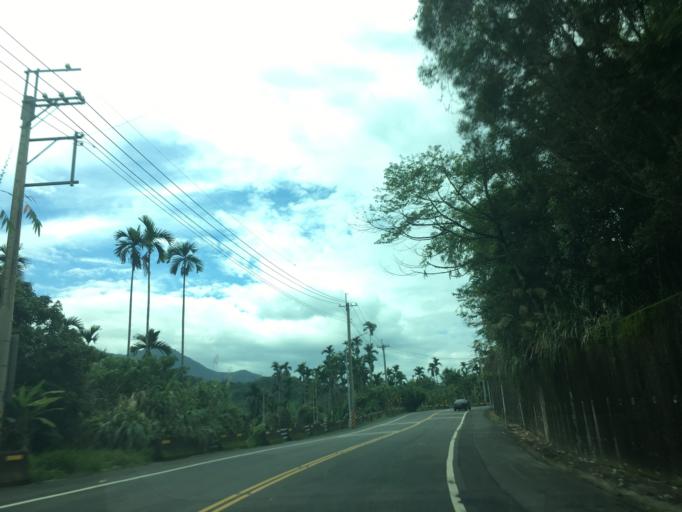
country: TW
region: Taiwan
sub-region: Yunlin
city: Douliu
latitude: 23.5759
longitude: 120.5641
